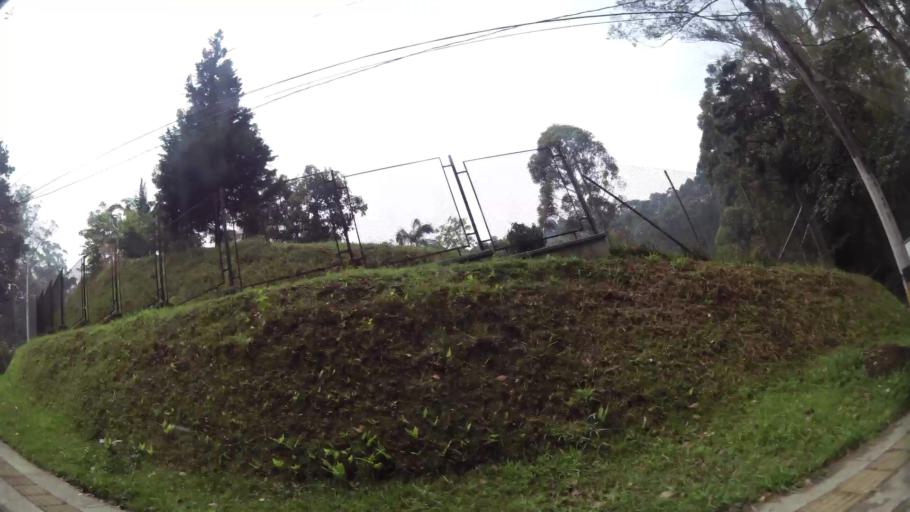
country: CO
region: Antioquia
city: Medellin
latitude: 6.2048
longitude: -75.5476
